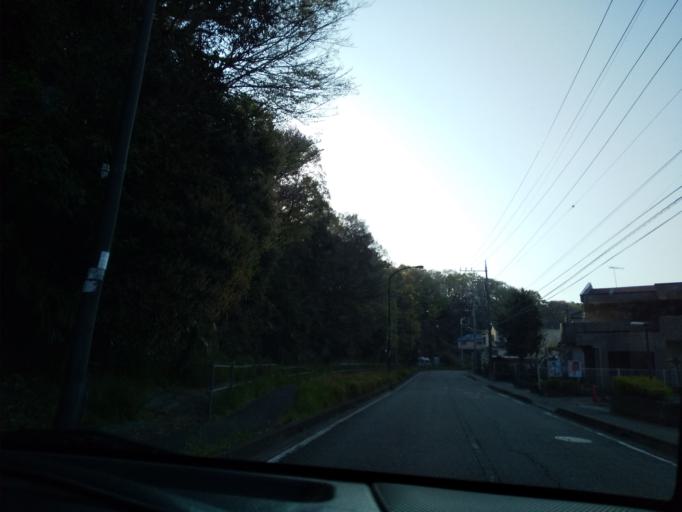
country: JP
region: Kanagawa
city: Zama
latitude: 35.5564
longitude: 139.3652
